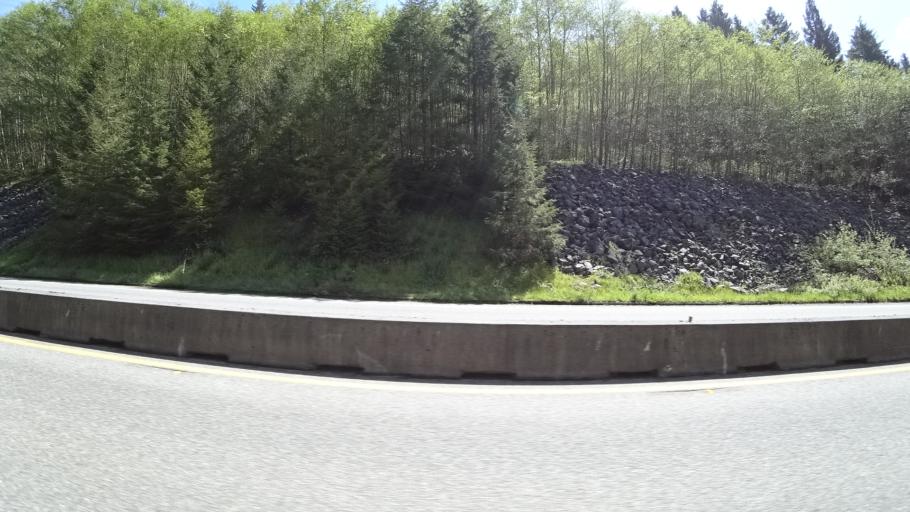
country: US
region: California
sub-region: Humboldt County
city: Westhaven-Moonstone
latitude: 41.3844
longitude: -123.9950
